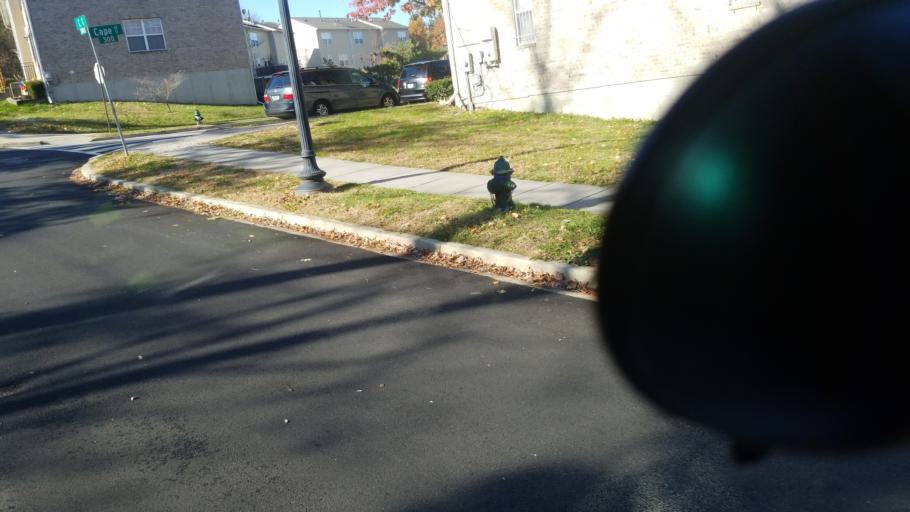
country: US
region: Maryland
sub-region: Prince George's County
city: Coral Hills
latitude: 38.8864
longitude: -76.9466
